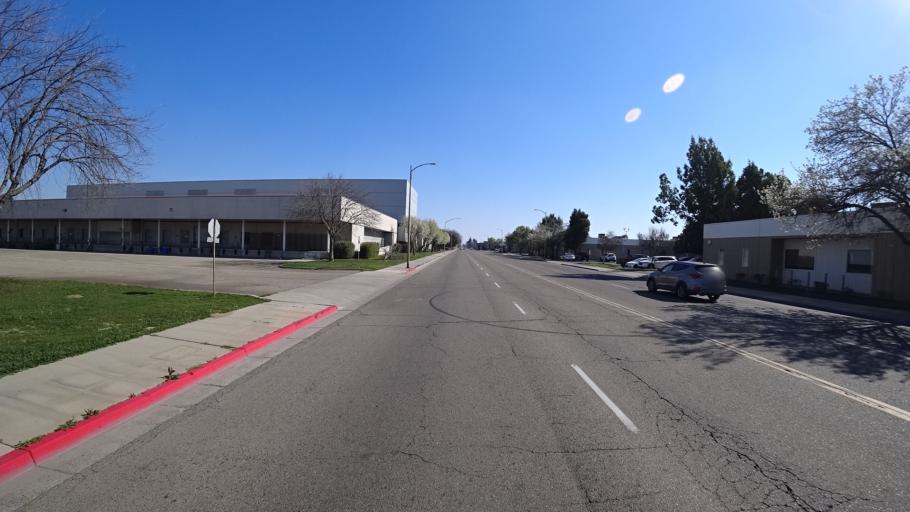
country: US
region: California
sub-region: Fresno County
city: Fresno
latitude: 36.7375
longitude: -119.8045
